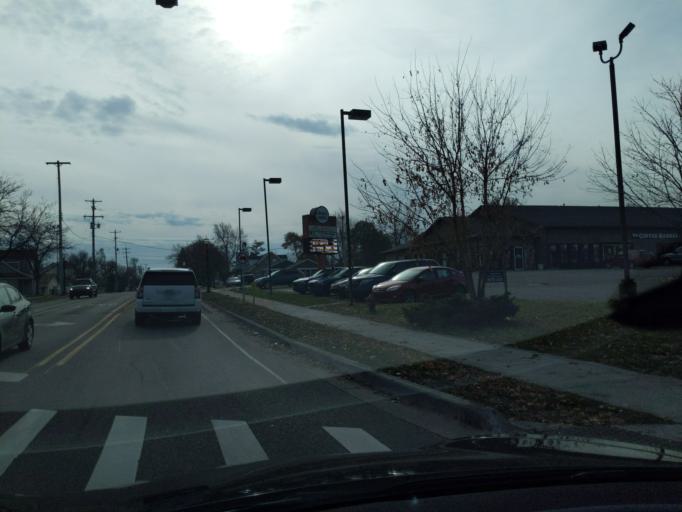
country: US
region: Michigan
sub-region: Ingham County
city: Holt
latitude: 42.6475
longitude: -84.5235
